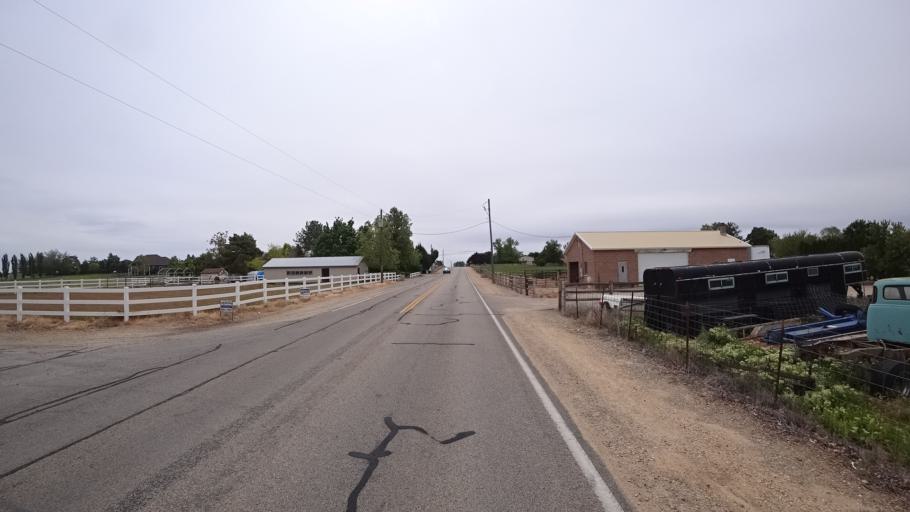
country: US
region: Idaho
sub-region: Ada County
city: Meridian
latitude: 43.5567
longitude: -116.3746
